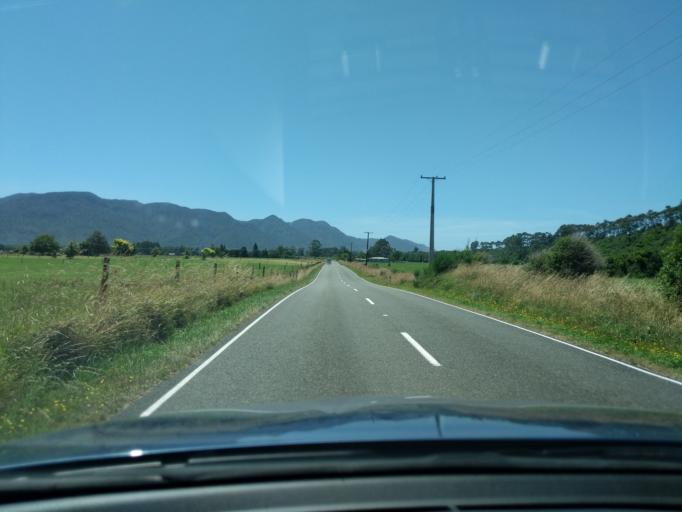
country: NZ
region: Tasman
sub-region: Tasman District
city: Takaka
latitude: -40.7204
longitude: 172.6382
